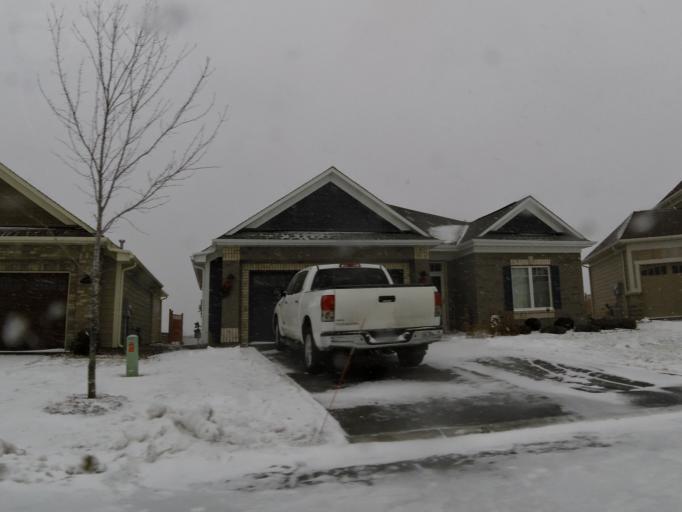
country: US
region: Minnesota
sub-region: Washington County
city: Oakdale
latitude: 44.9612
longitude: -92.9316
